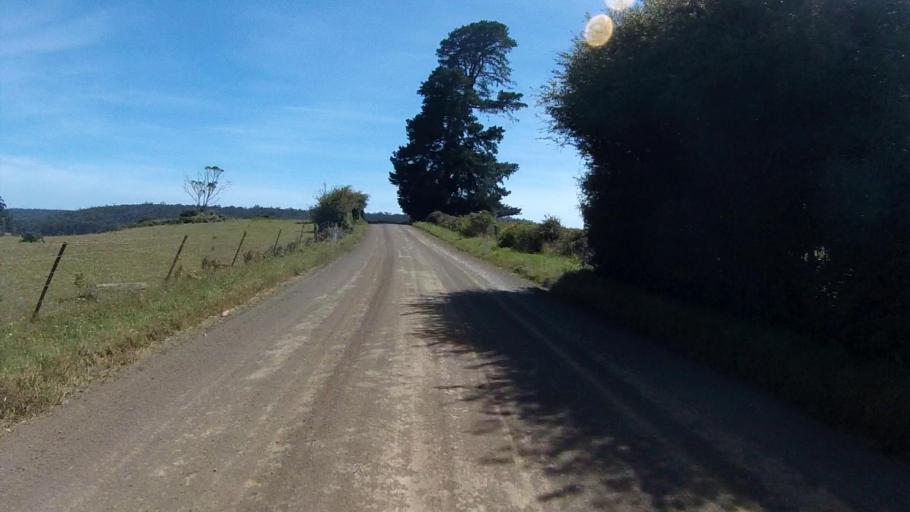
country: AU
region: Tasmania
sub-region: Sorell
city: Sorell
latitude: -42.7232
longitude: 147.7438
